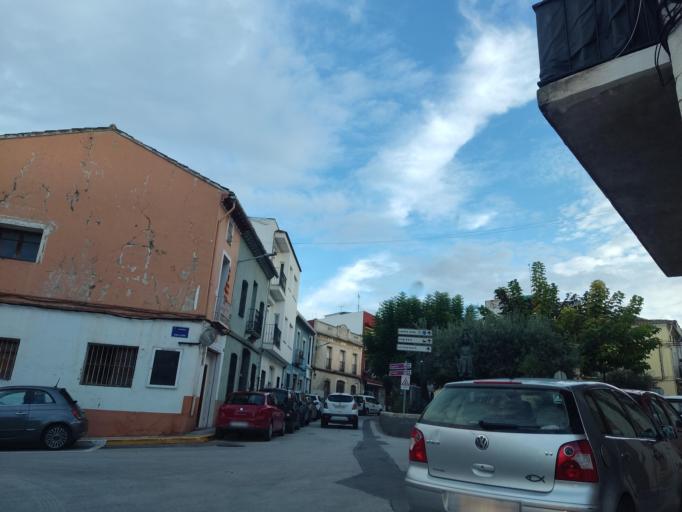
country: ES
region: Valencia
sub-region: Provincia de Alicante
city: Pedreguer
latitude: 38.7951
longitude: 0.0332
